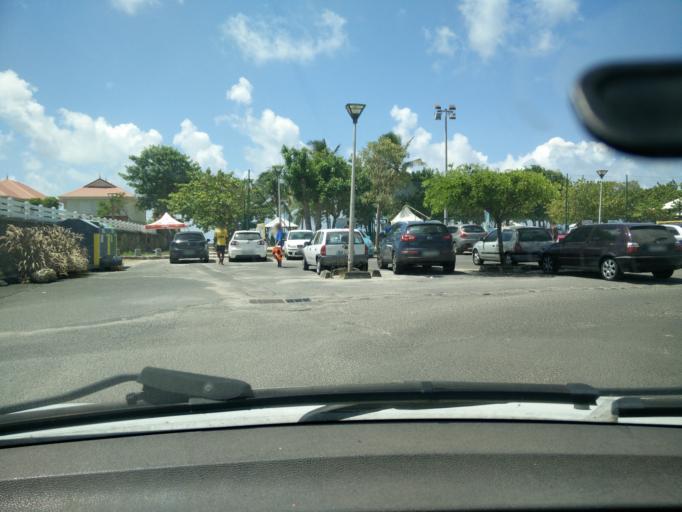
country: GP
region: Guadeloupe
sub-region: Guadeloupe
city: Le Moule
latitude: 16.3322
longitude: -61.3394
